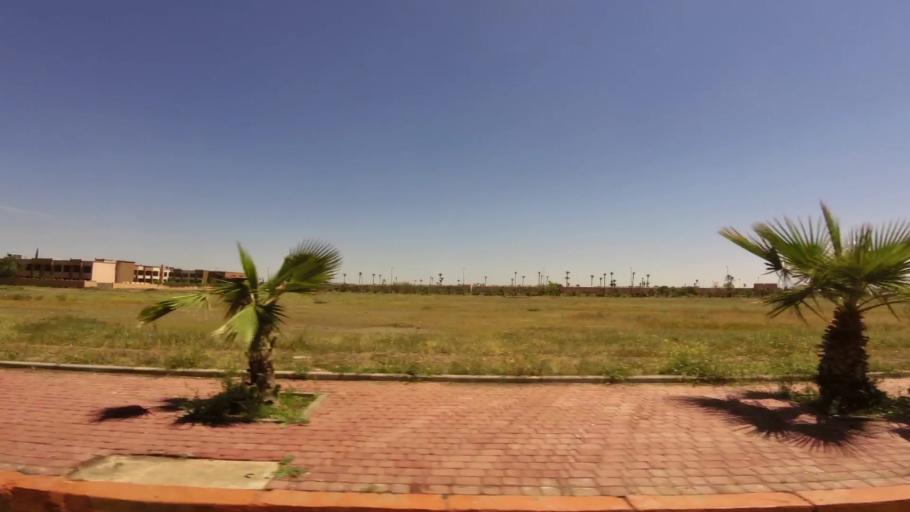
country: MA
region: Marrakech-Tensift-Al Haouz
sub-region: Marrakech
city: Marrakesh
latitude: 31.5839
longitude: -7.9857
